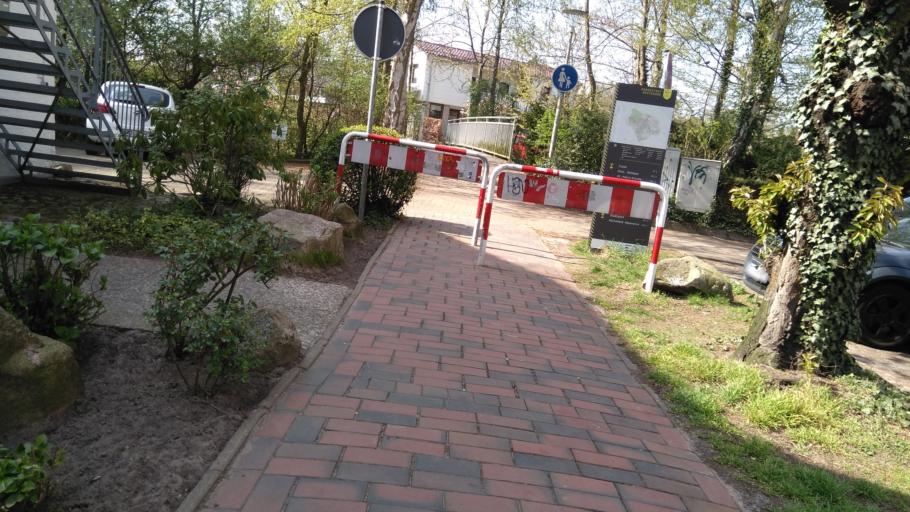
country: DE
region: Lower Saxony
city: Buxtehude
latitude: 53.4765
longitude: 9.6970
